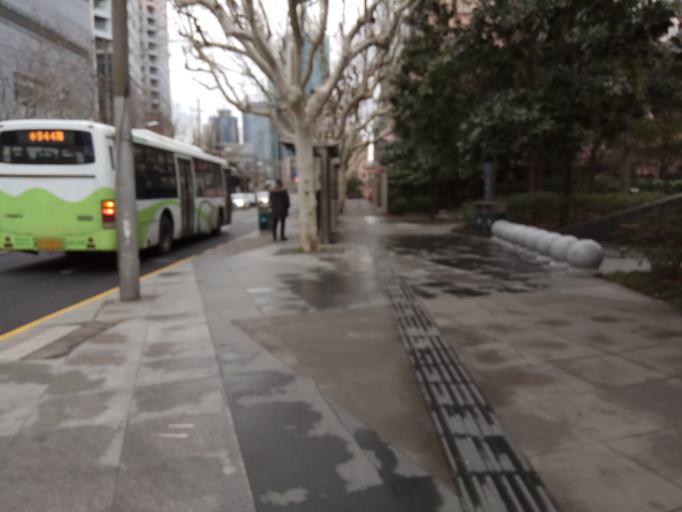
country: CN
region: Shanghai Shi
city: Changning
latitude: 31.2072
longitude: 121.4007
